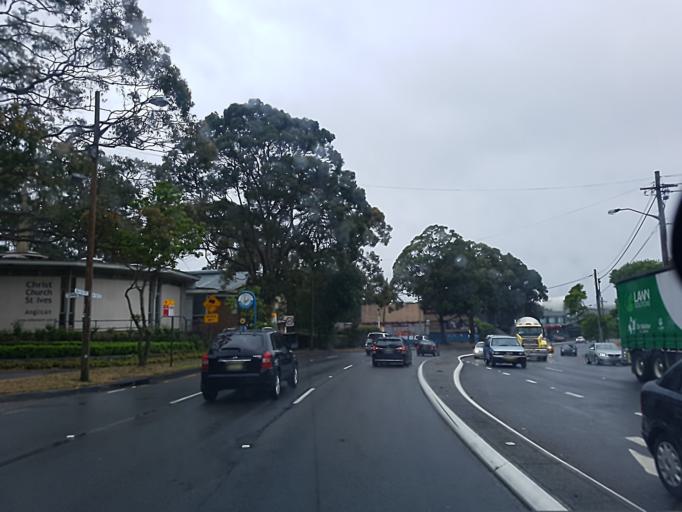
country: AU
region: New South Wales
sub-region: City of Sydney
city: Pymble
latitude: -33.7317
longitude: 151.1564
